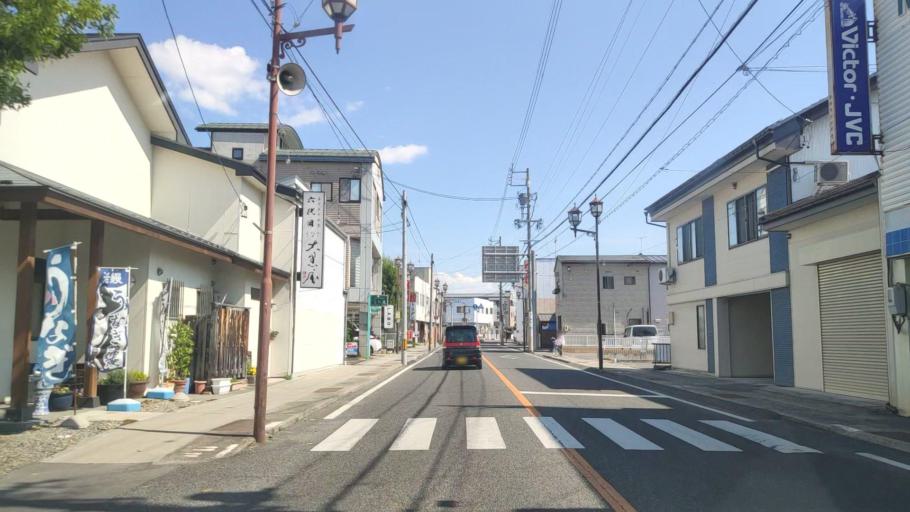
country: JP
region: Nagano
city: Toyoshina
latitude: 36.2992
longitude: 137.9048
